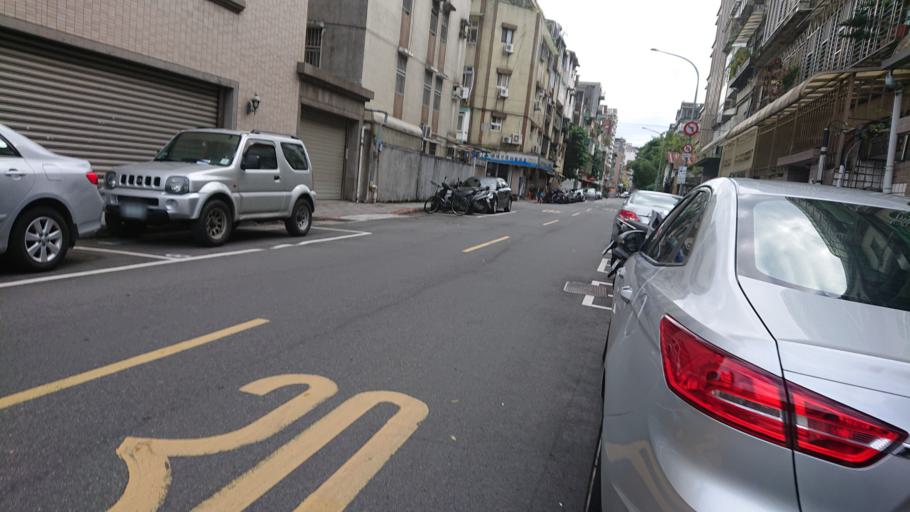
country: TW
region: Taipei
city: Taipei
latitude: 25.0311
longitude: 121.5405
